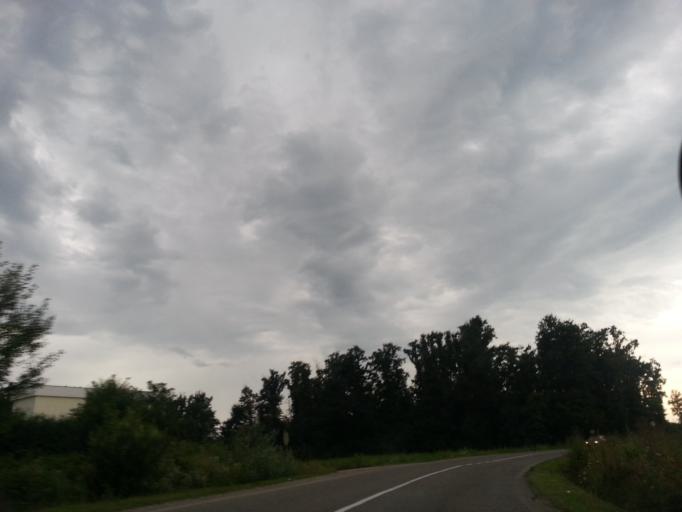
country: BA
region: Republika Srpska
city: Velika Obarska
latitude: 44.7674
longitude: 19.1315
